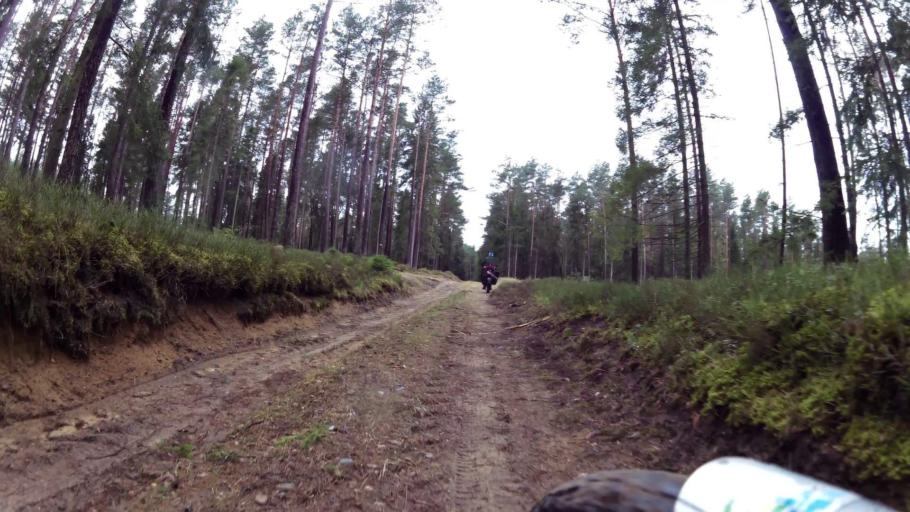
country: PL
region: Pomeranian Voivodeship
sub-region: Powiat bytowski
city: Borzytuchom
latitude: 54.2616
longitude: 17.3364
